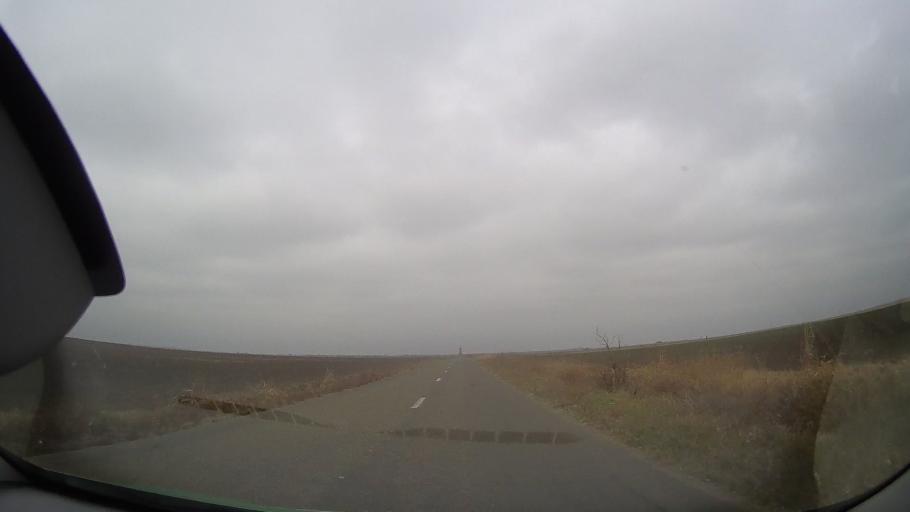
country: RO
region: Buzau
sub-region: Comuna Bradeanu
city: Bradeanu
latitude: 44.8948
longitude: 26.8734
